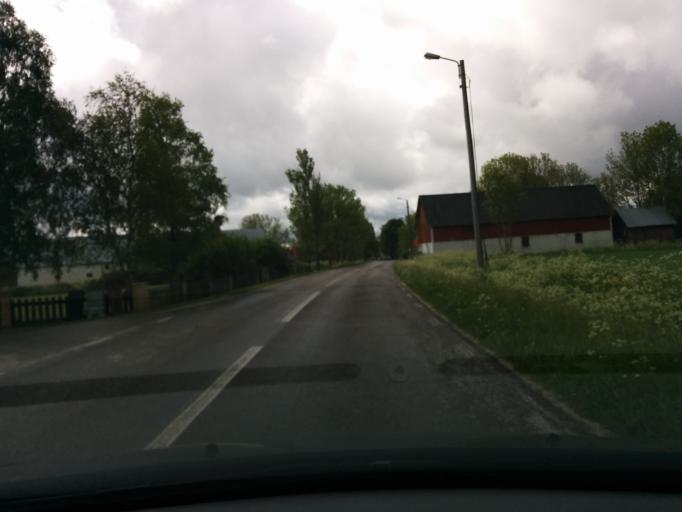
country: SE
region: Gotland
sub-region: Gotland
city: Slite
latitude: 57.5818
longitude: 18.7296
